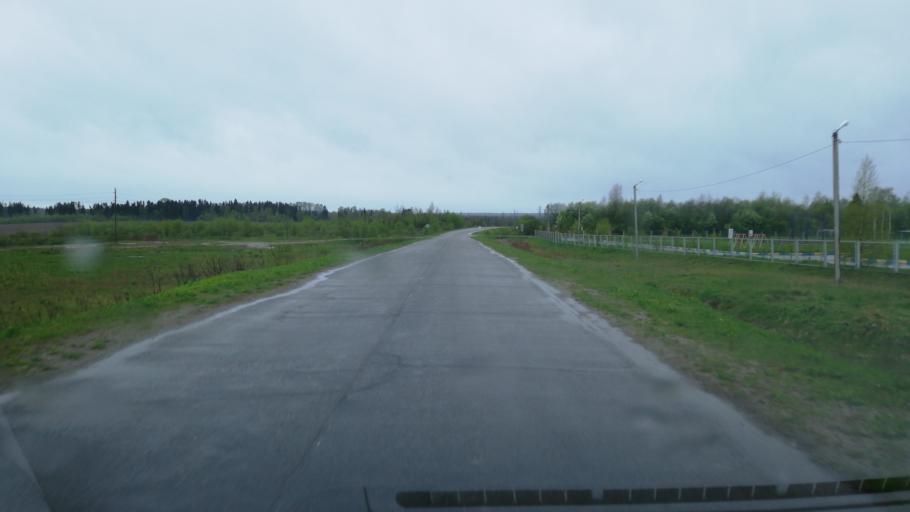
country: RU
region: Jaroslavl
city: Danilov
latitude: 57.9914
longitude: 40.1788
